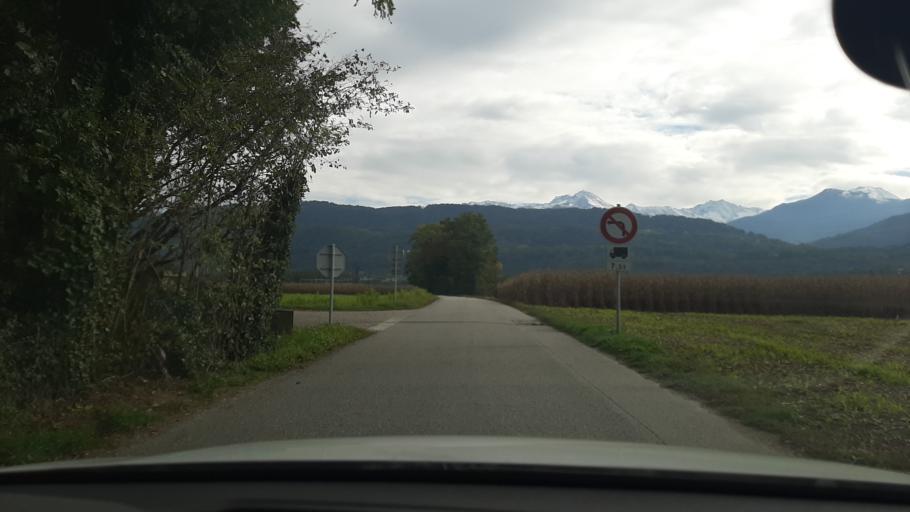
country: FR
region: Rhone-Alpes
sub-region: Departement de la Savoie
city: Montmelian
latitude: 45.4714
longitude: 6.0382
